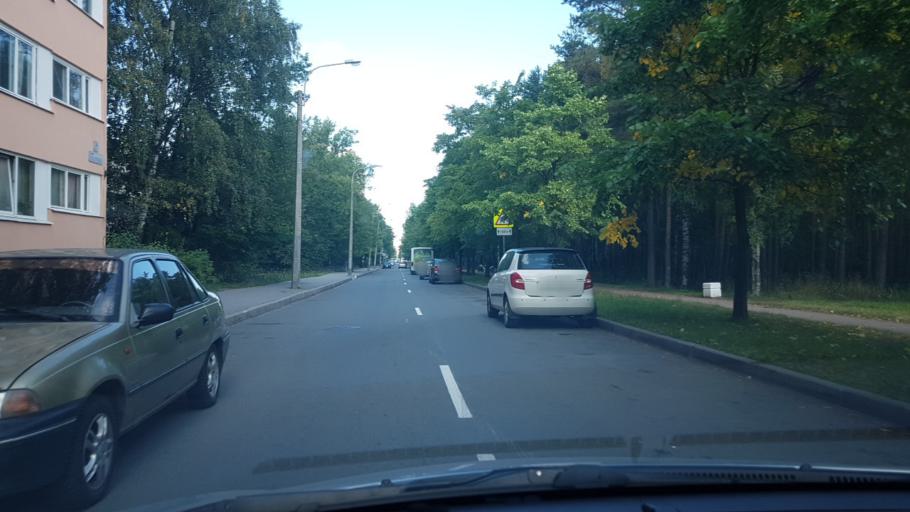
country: RU
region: St.-Petersburg
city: Dachnoye
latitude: 59.8312
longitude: 30.2266
